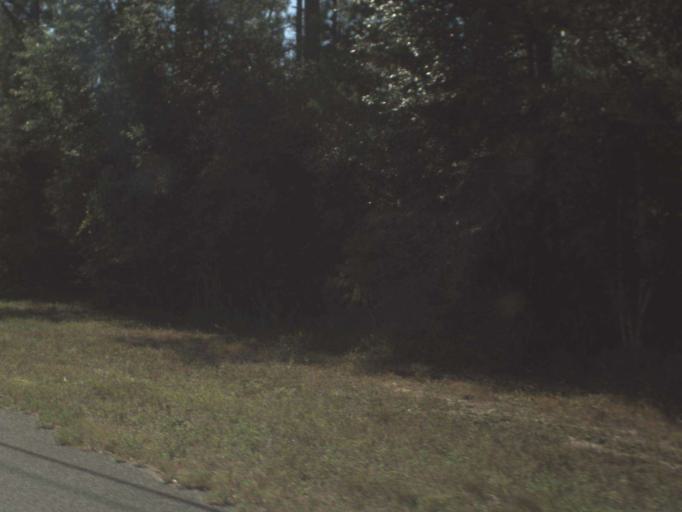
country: US
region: Florida
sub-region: Walton County
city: DeFuniak Springs
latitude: 30.7888
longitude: -86.1206
